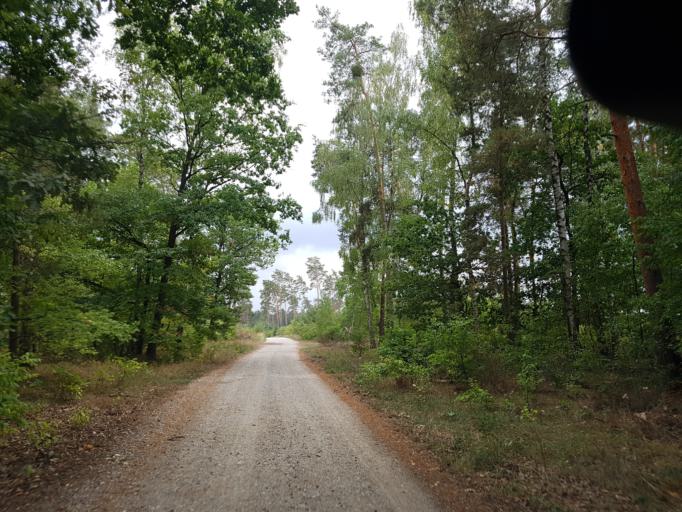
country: DE
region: Saxony-Anhalt
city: Rosslau
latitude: 52.0238
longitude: 12.2900
